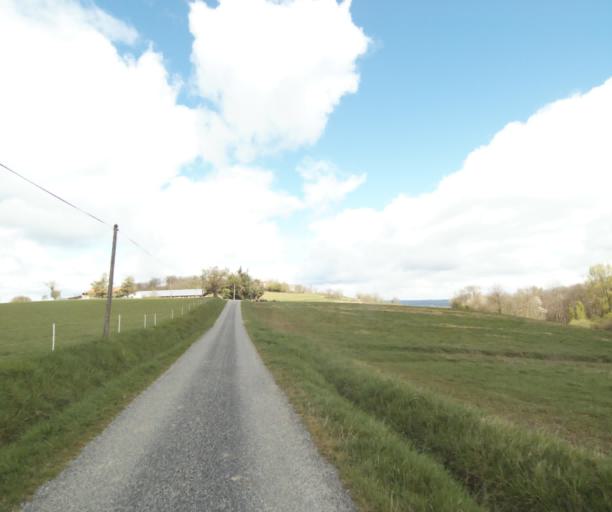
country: FR
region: Midi-Pyrenees
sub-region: Departement de l'Ariege
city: Saverdun
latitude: 43.1854
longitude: 1.5781
